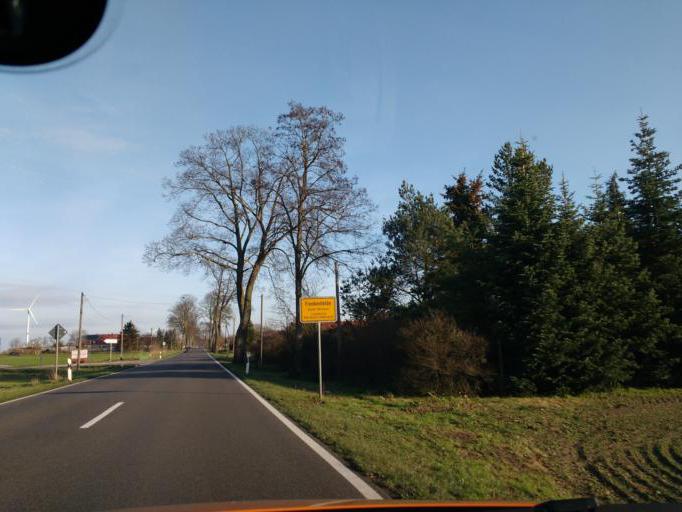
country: DE
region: Brandenburg
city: Protzel
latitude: 52.6678
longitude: 14.0598
